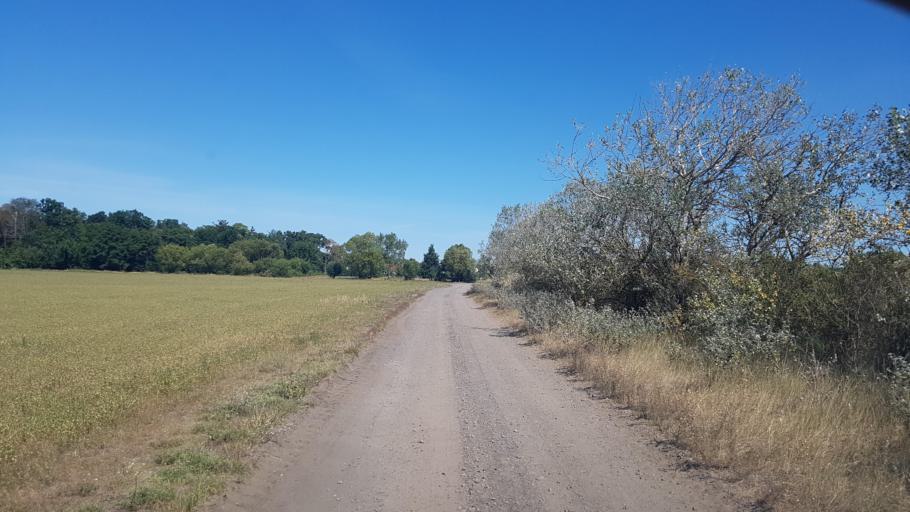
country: DE
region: Brandenburg
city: Golzow
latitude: 52.2527
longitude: 12.6627
